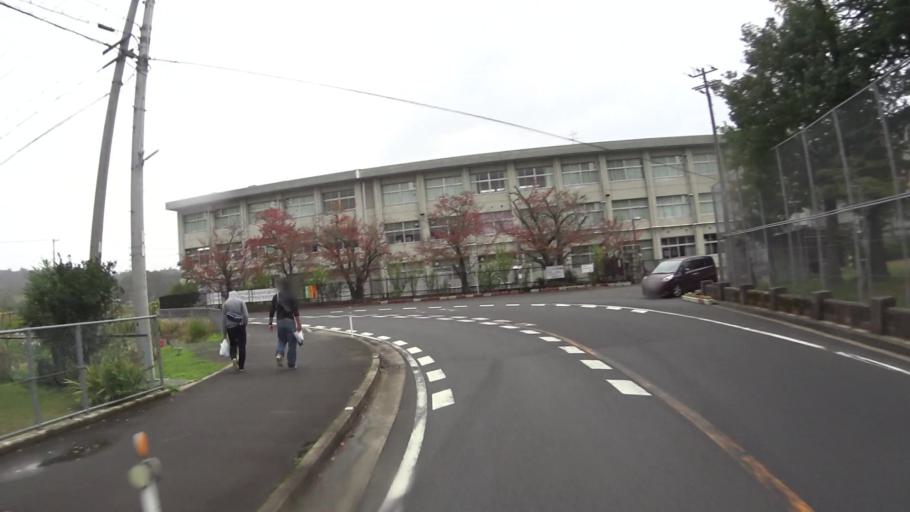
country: JP
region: Kyoto
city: Miyazu
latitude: 35.5497
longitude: 135.2348
